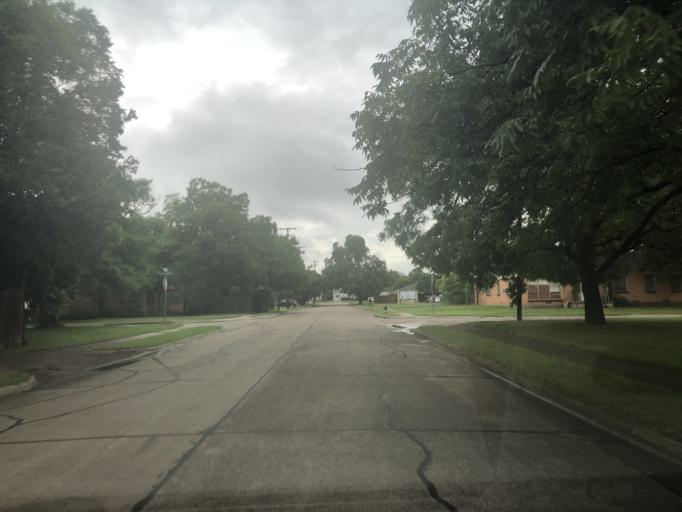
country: US
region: Texas
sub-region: Dallas County
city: Irving
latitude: 32.7995
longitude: -96.9496
